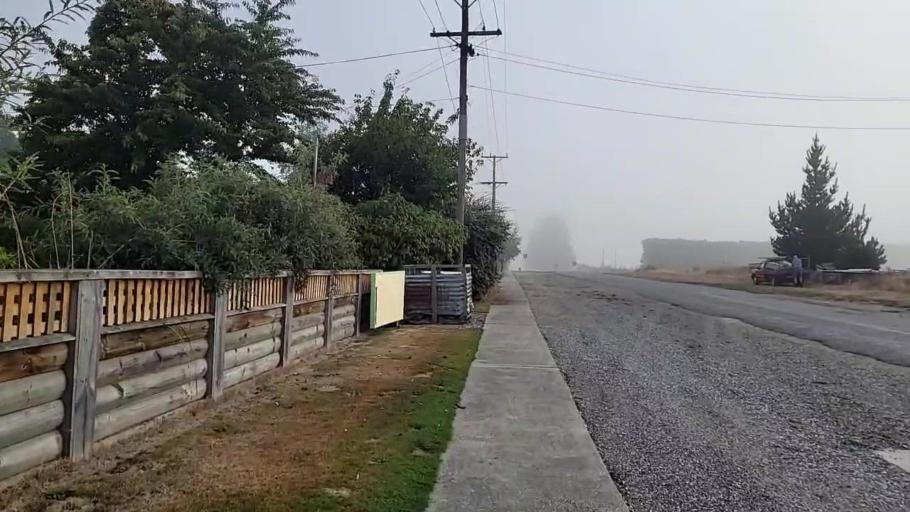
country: NZ
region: Southland
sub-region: Gore District
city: Gore
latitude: -45.6315
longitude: 169.3616
